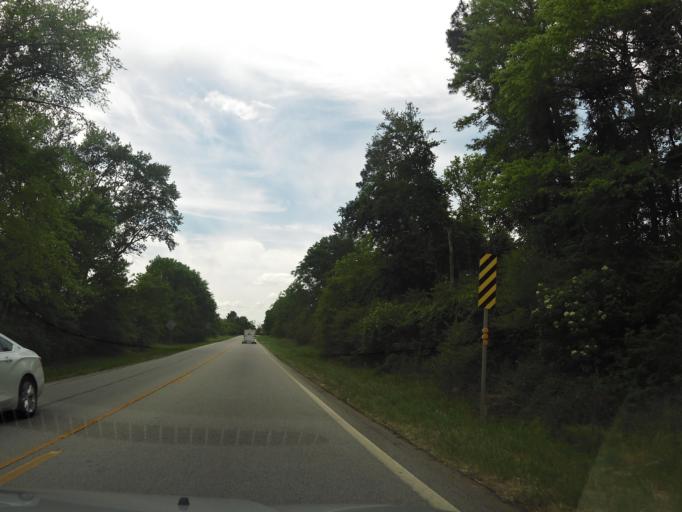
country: US
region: Georgia
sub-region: Emanuel County
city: Swainsboro
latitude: 32.5130
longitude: -82.2673
